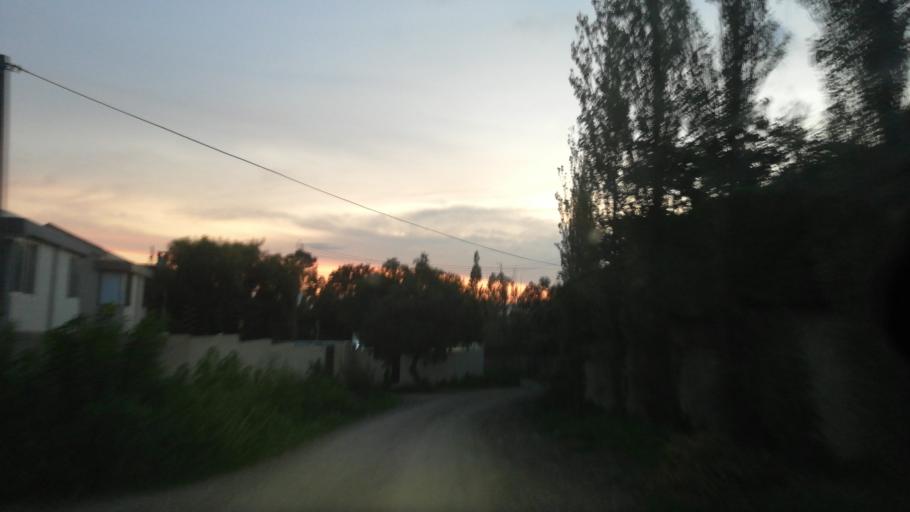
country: BO
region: Cochabamba
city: Cochabamba
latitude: -17.3338
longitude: -66.2085
